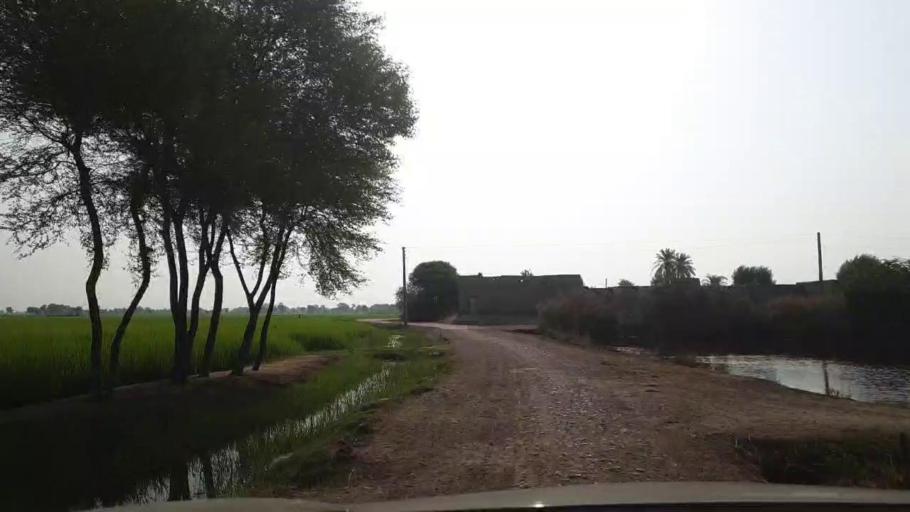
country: PK
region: Sindh
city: Larkana
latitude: 27.4923
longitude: 68.2103
